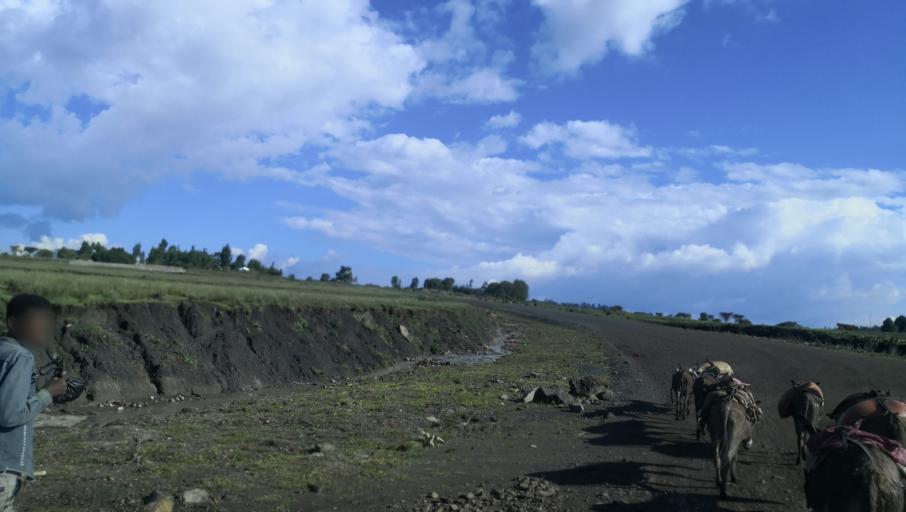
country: ET
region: Oromiya
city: Tulu Bolo
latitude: 8.5781
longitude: 38.2407
